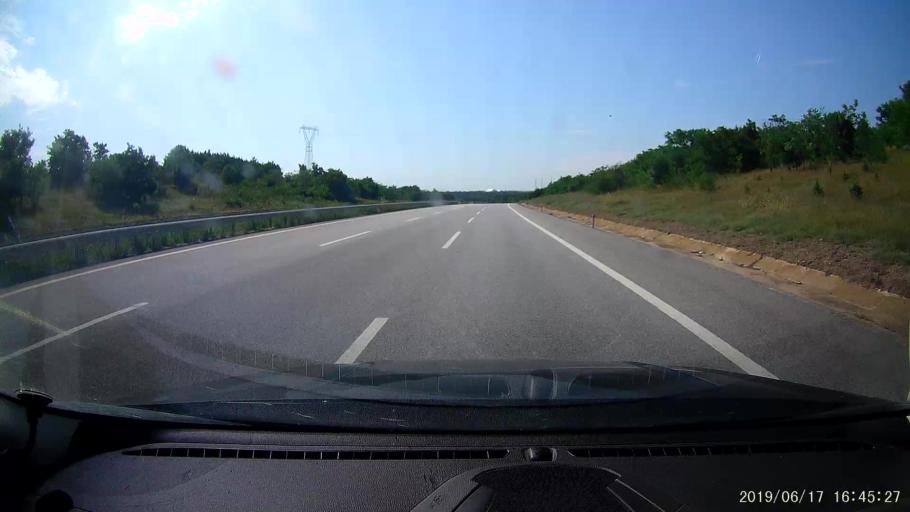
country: TR
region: Kirklareli
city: Babaeski
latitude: 41.4885
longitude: 27.2325
